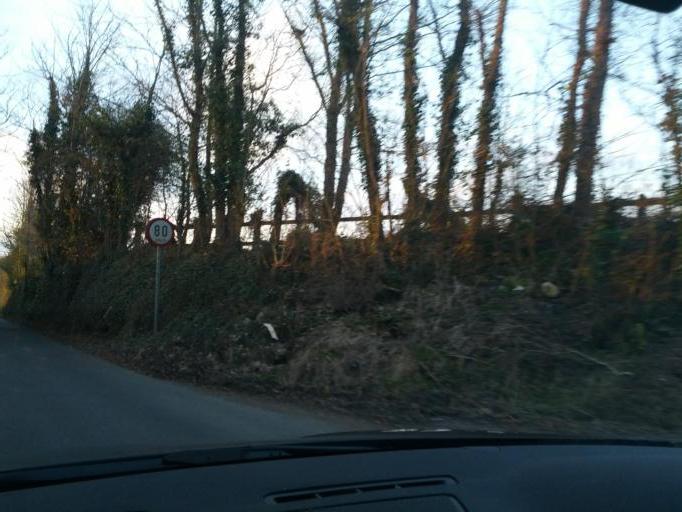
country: IE
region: Munster
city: Nenagh Bridge
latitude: 52.9346
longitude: -8.2401
